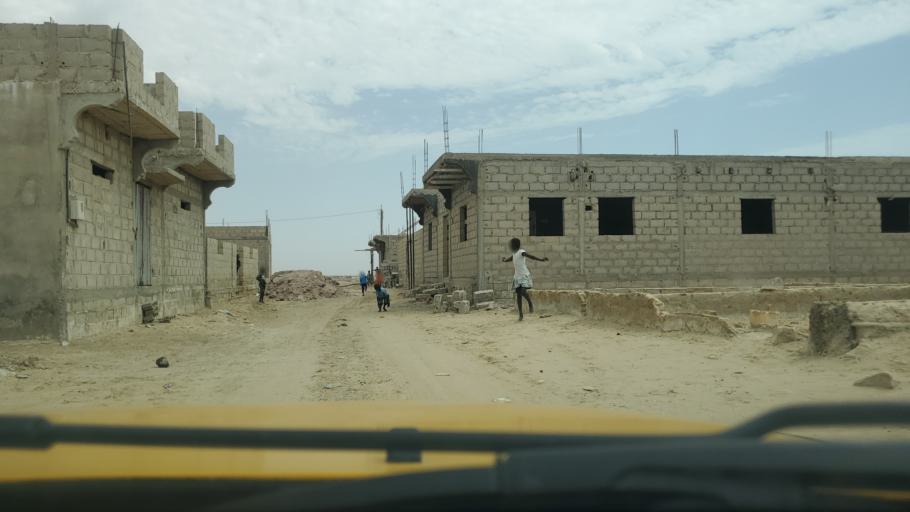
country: SN
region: Saint-Louis
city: Saint-Louis
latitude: 16.0336
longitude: -16.4620
